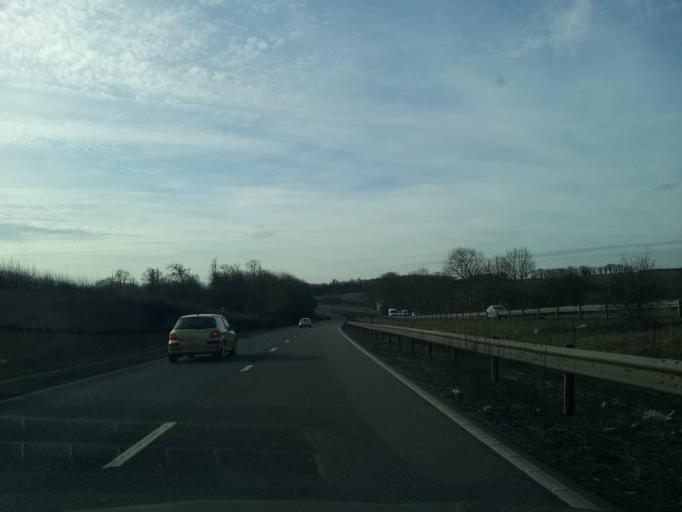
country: GB
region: England
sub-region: Cambridgeshire
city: Buckden
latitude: 52.2843
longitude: -0.2578
